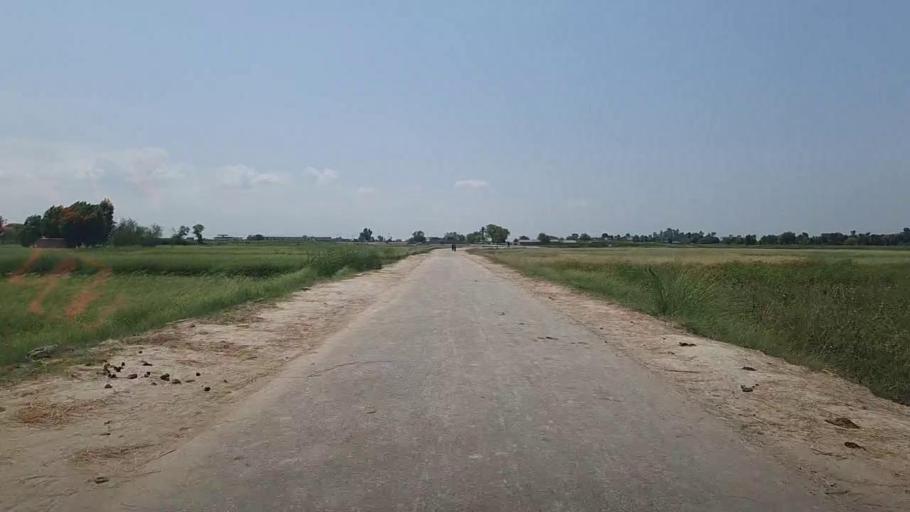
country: PK
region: Sindh
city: Ubauro
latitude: 28.1891
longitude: 69.7999
